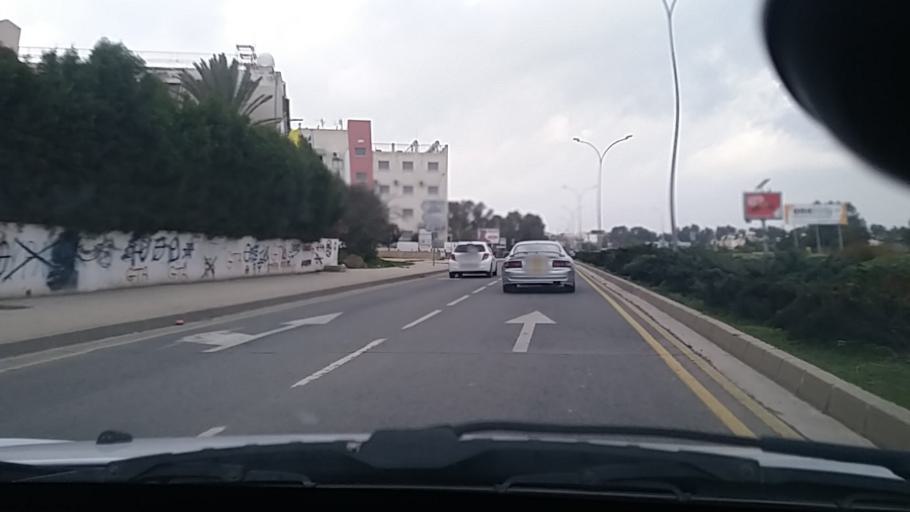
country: CY
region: Lefkosia
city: Tseri
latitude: 35.1291
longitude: 33.3176
